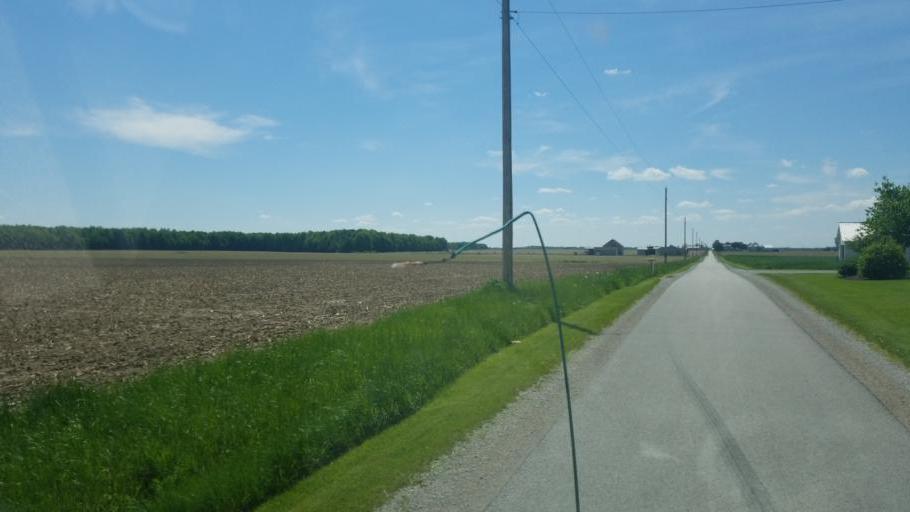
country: US
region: Ohio
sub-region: Crawford County
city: Bucyrus
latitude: 41.0083
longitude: -82.9407
